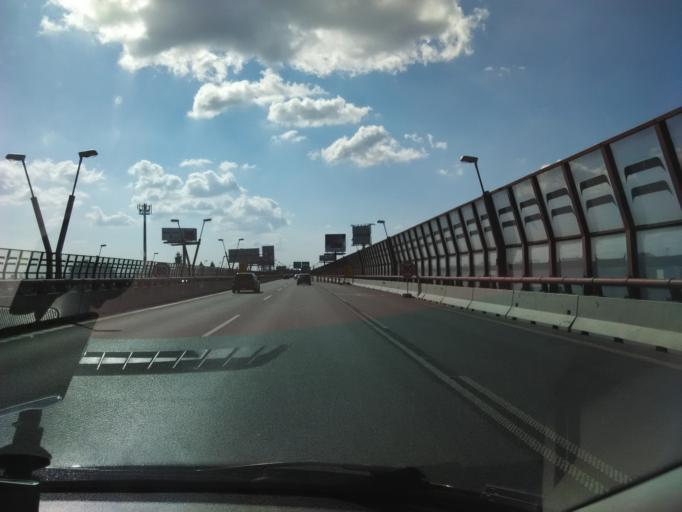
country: SK
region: Bratislavsky
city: Bratislava
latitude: 48.1582
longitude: 17.1820
